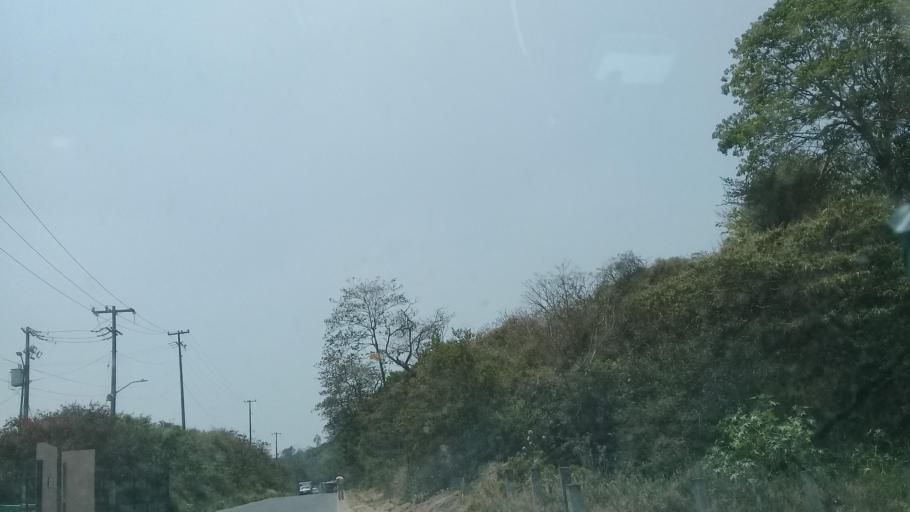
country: MX
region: Veracruz
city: El Castillo
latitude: 19.5543
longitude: -96.8553
